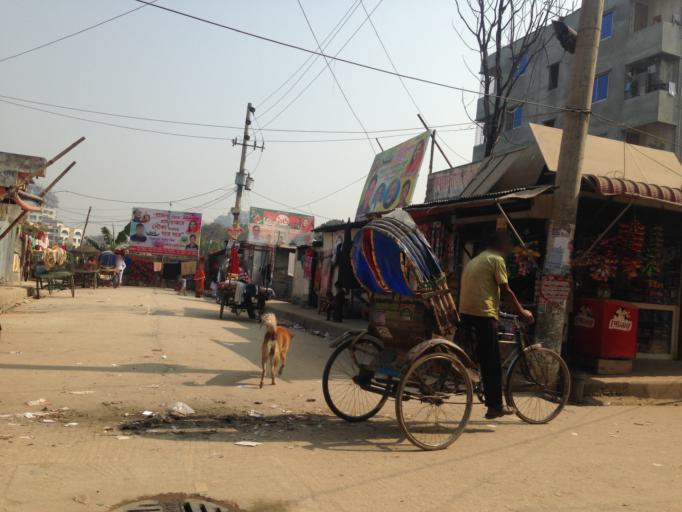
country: BD
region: Dhaka
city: Azimpur
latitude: 23.8057
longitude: 90.3469
